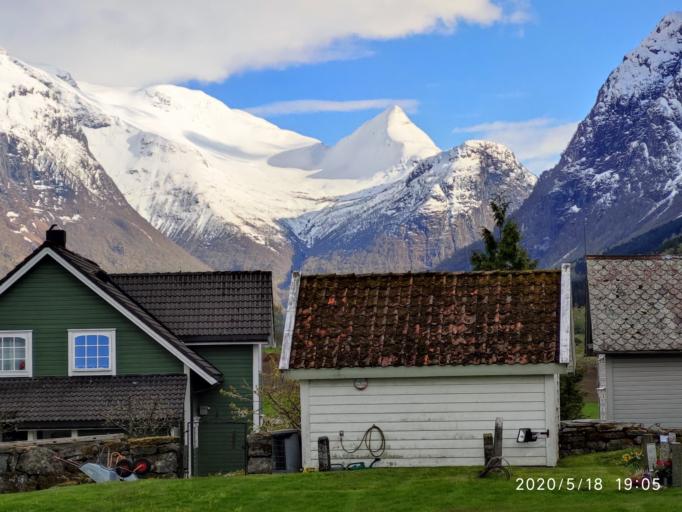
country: NO
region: Sogn og Fjordane
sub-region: Stryn
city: Stryn
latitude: 61.8344
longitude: 6.8053
